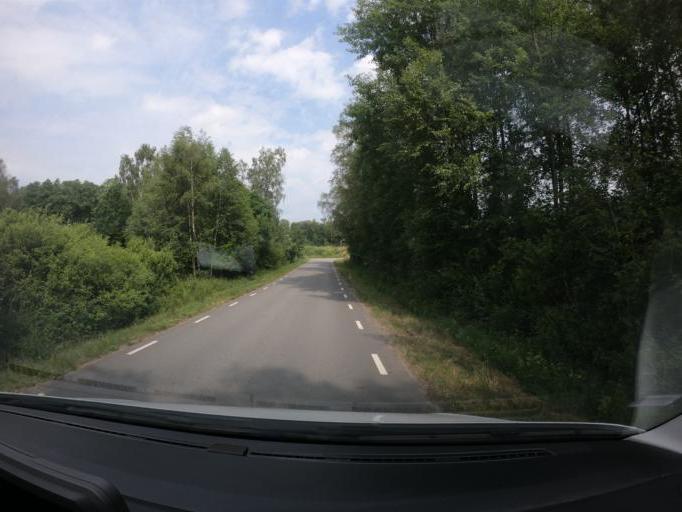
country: SE
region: Skane
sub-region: Hassleholms Kommun
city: Bjarnum
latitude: 56.2769
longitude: 13.7111
